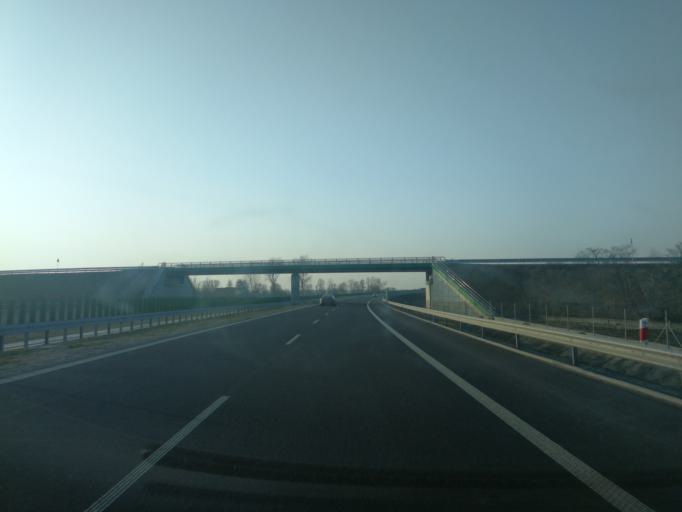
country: PL
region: Pomeranian Voivodeship
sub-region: Powiat nowodworski
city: Nowy Dwor Gdanski
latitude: 54.1758
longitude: 19.1907
